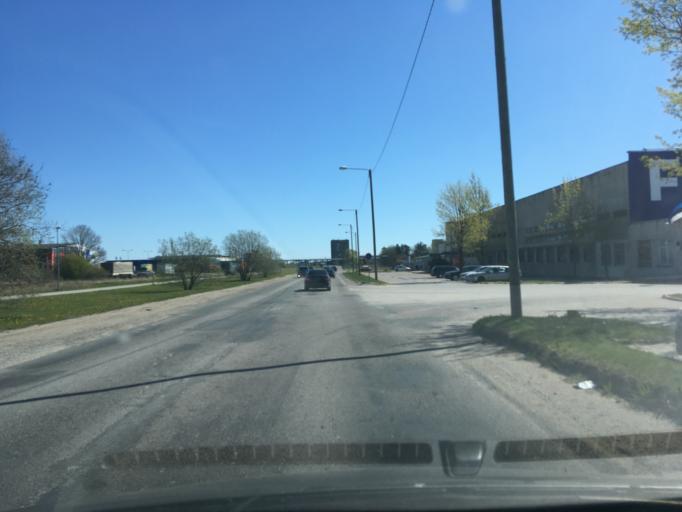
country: EE
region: Harju
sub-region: Joelaehtme vald
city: Loo
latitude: 59.4592
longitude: 24.9311
